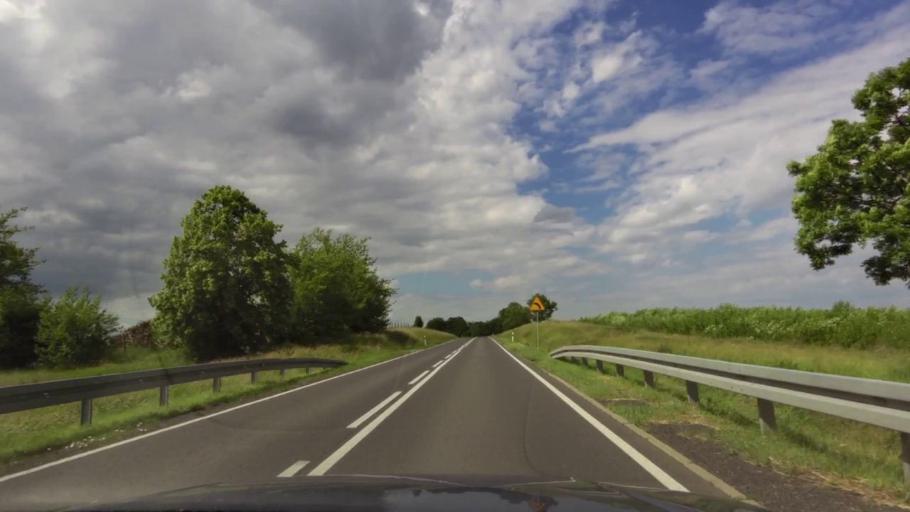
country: PL
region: West Pomeranian Voivodeship
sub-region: Powiat gryfinski
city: Mieszkowice
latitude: 52.8468
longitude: 14.4920
